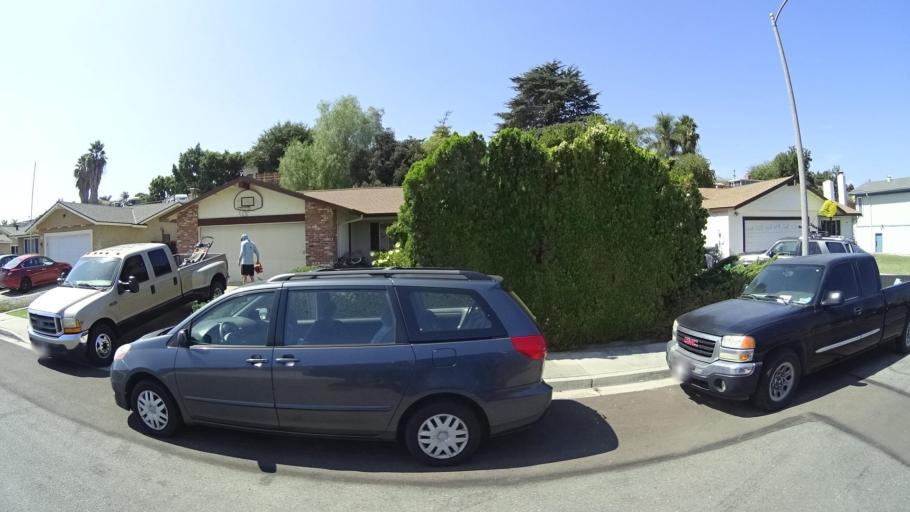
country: US
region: California
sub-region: San Diego County
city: Spring Valley
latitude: 32.7375
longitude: -116.9834
